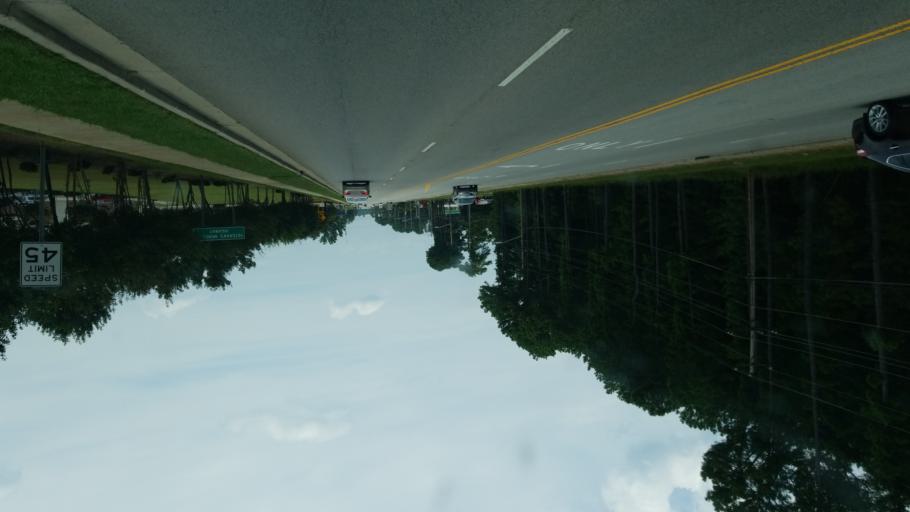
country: US
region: South Carolina
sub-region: York County
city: Newport
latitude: 34.9532
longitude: -81.0886
